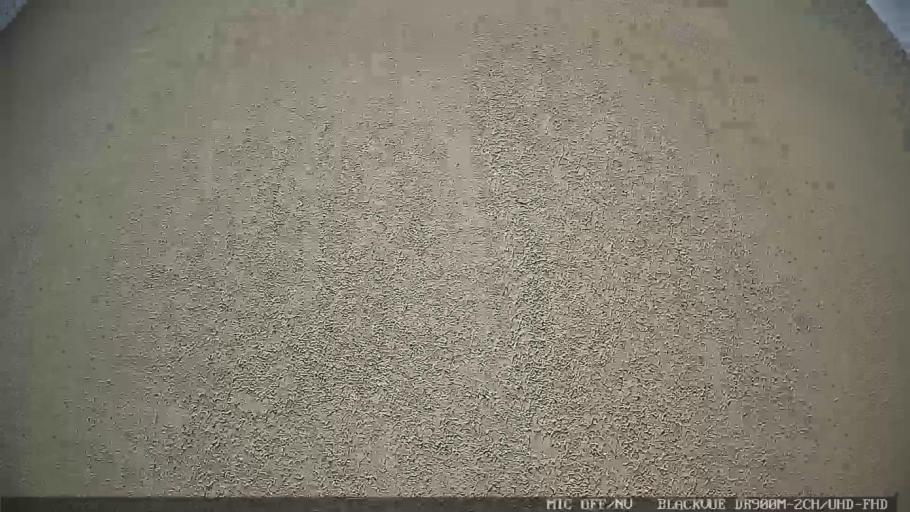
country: BR
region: Sao Paulo
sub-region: Sao Caetano Do Sul
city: Sao Caetano do Sul
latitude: -23.5678
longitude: -46.5598
